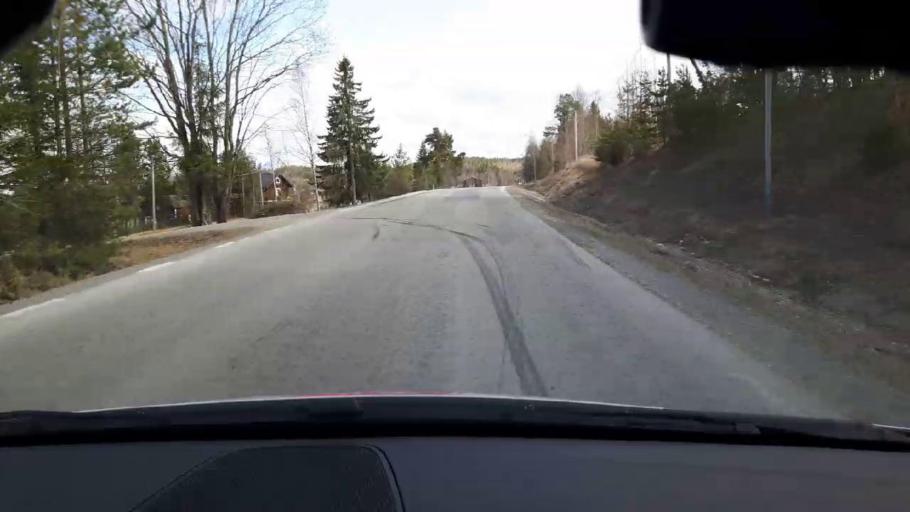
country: SE
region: Jaemtland
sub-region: Bergs Kommun
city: Hoverberg
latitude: 62.7803
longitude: 14.5131
